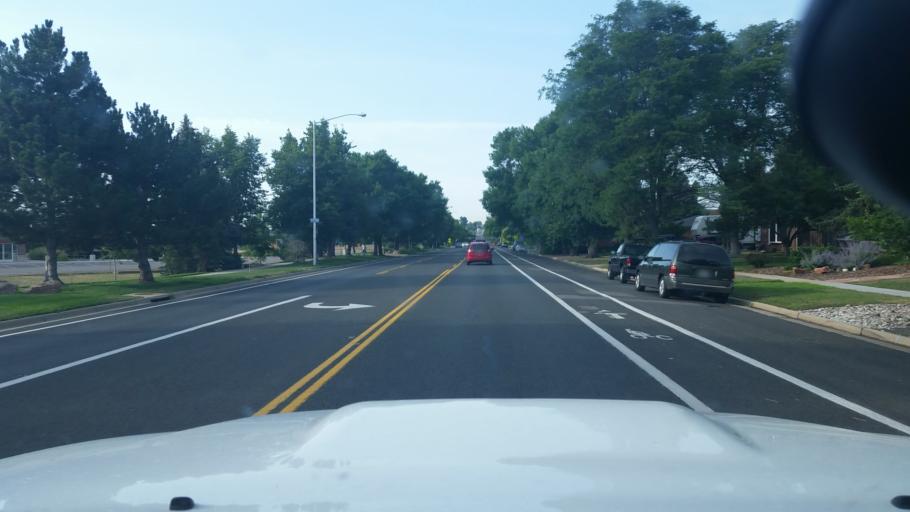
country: US
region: Colorado
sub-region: Broomfield County
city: Broomfield
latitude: 39.9240
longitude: -105.0719
